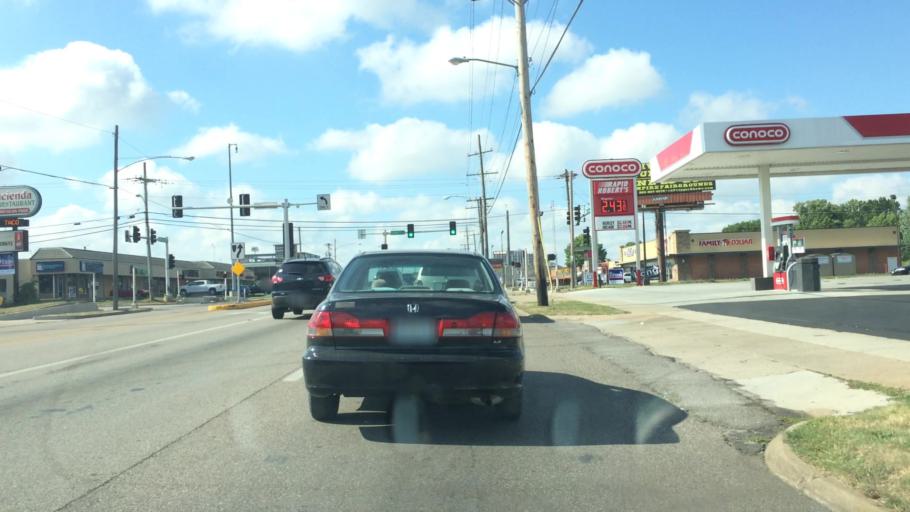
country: US
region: Missouri
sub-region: Greene County
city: Springfield
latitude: 37.1896
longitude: -93.2623
